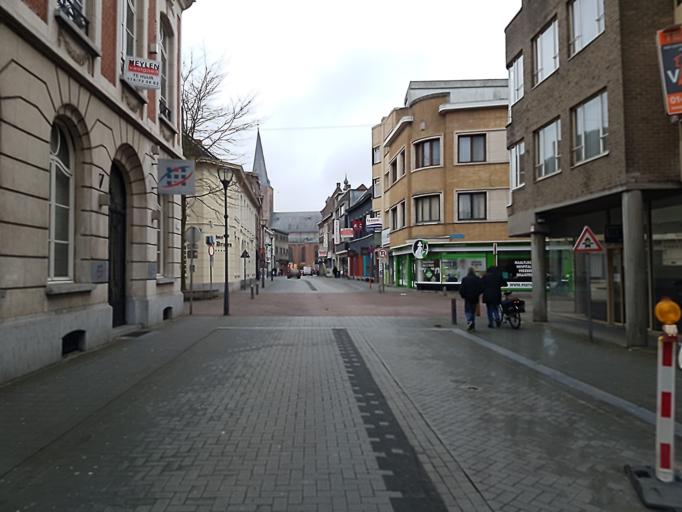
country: BE
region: Flanders
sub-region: Provincie Antwerpen
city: Turnhout
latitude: 51.3207
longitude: 4.9489
